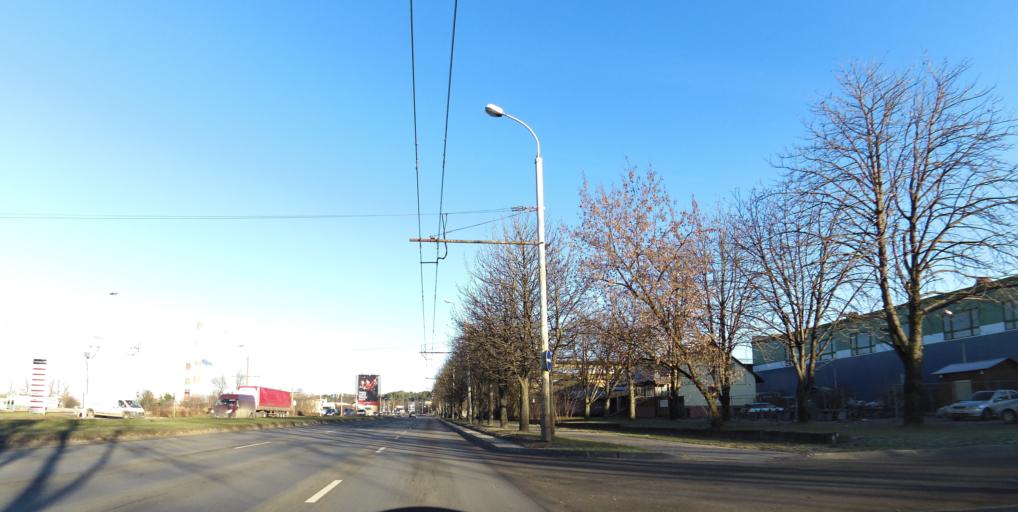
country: LT
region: Vilnius County
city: Vilkpede
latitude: 54.6562
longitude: 25.2281
